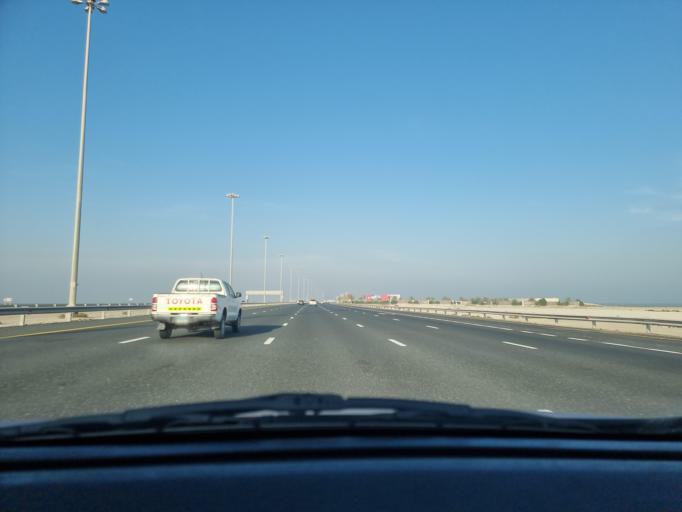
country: AE
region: Abu Dhabi
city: Abu Dhabi
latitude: 24.5088
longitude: 54.5579
